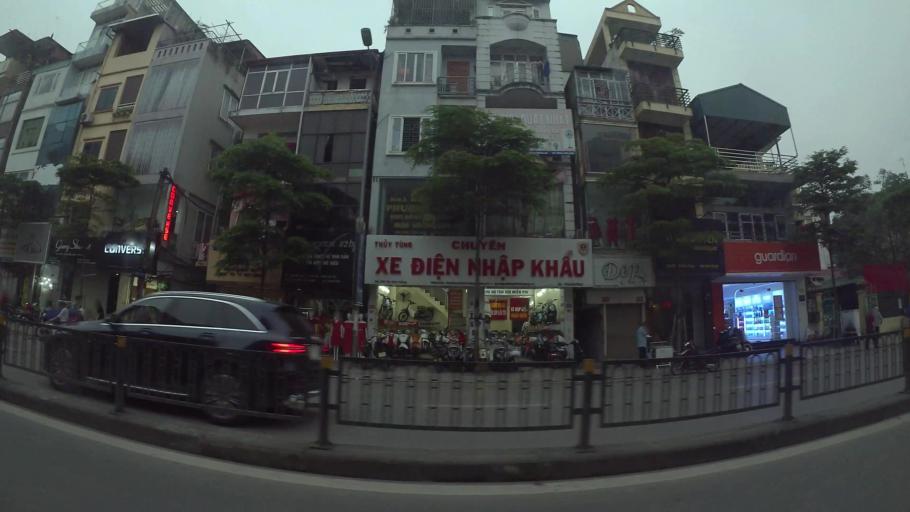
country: VN
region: Ha Noi
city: Dong Da
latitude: 21.0223
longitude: 105.8317
